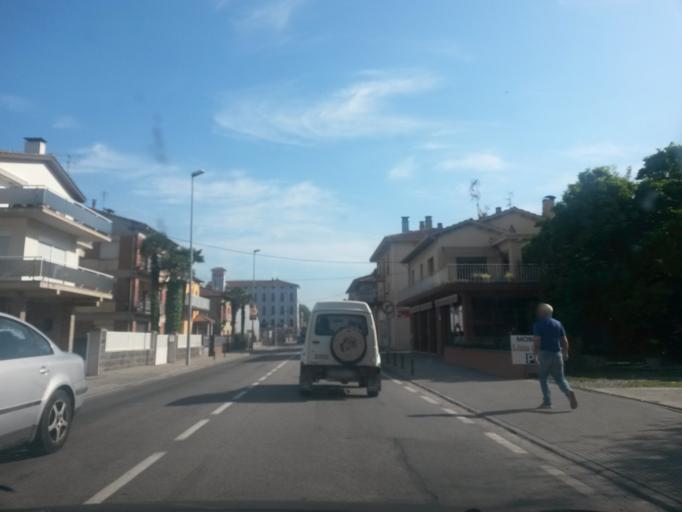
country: ES
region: Catalonia
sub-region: Provincia de Girona
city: Bas
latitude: 42.1446
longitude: 2.4587
